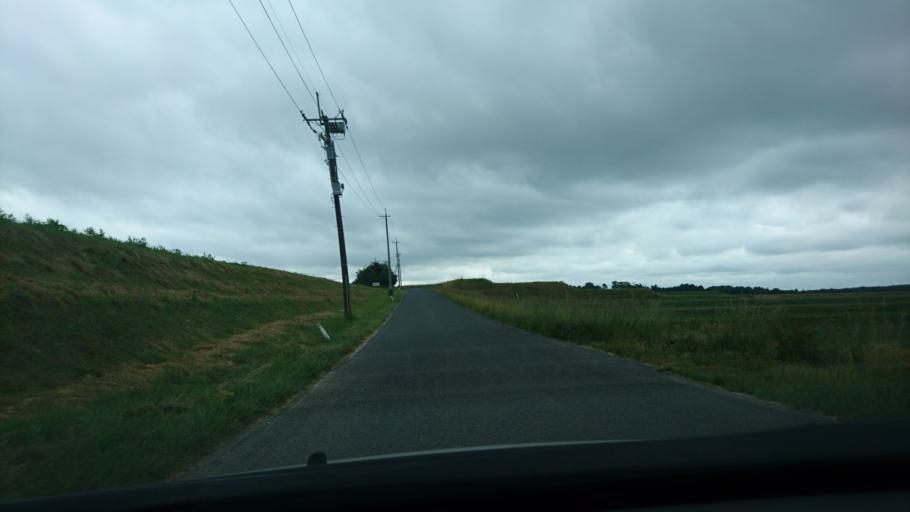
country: JP
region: Iwate
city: Ichinoseki
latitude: 38.8850
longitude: 141.1954
